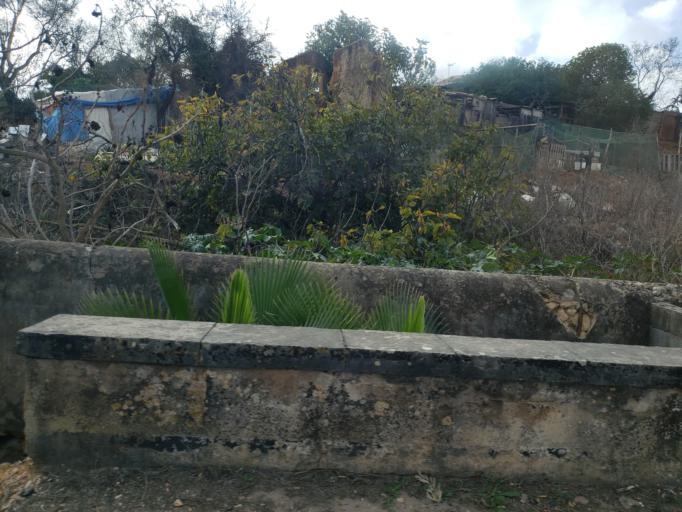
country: PT
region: Faro
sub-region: Portimao
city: Portimao
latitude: 37.1520
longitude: -8.5557
